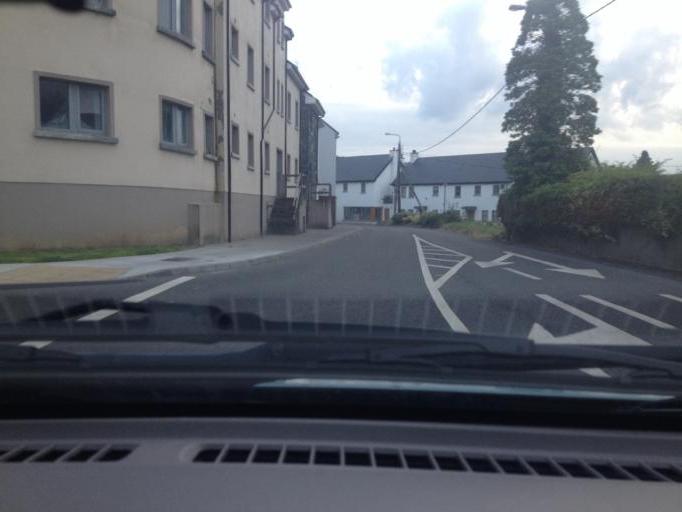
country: IE
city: Ballisodare
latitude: 54.2119
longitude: -8.5060
